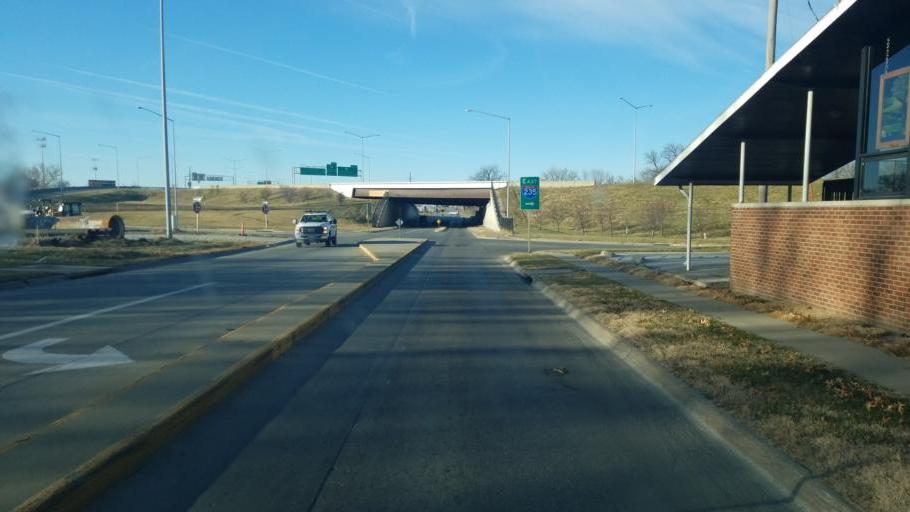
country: US
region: Iowa
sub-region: Polk County
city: Des Moines
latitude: 41.6049
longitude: -93.5779
